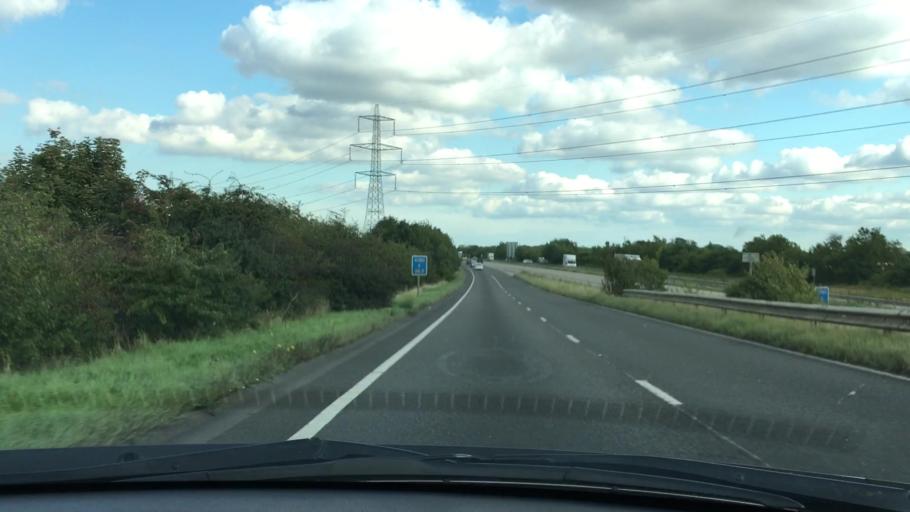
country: GB
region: England
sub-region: North East Lincolnshire
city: Immingham
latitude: 53.5974
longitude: -0.1944
